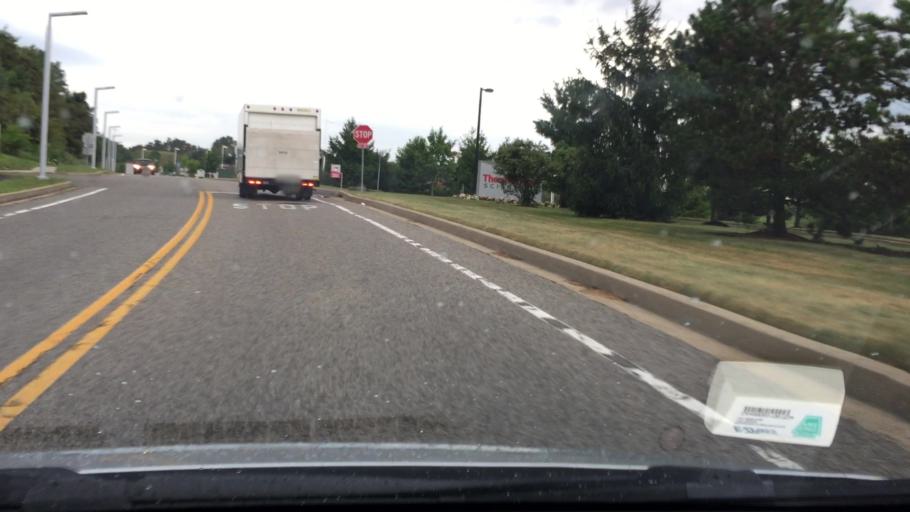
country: US
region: Pennsylvania
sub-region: Allegheny County
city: Enlow
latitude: 40.4698
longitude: -80.2158
